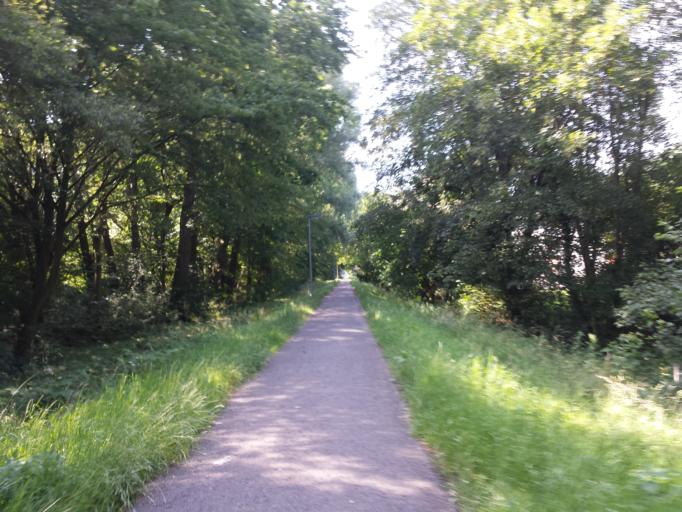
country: DE
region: Lower Saxony
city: Stuhr
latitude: 53.0806
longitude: 8.7588
